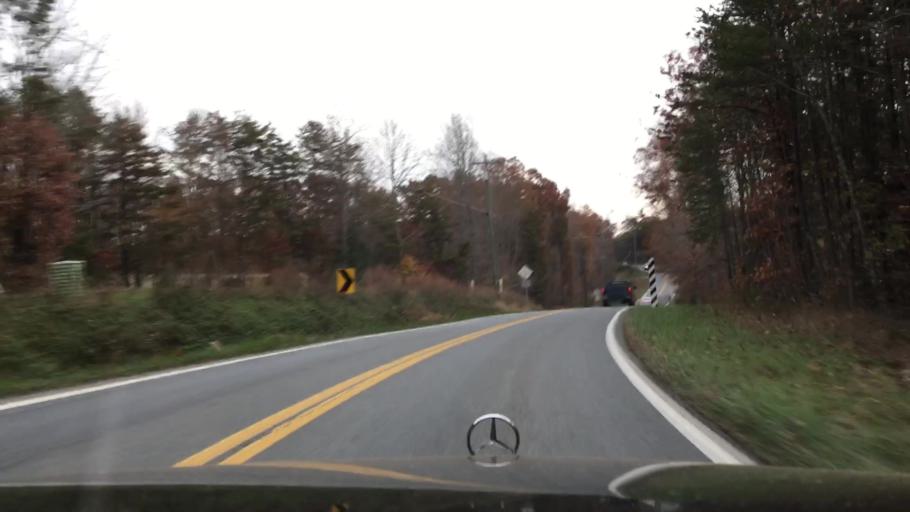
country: US
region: Virginia
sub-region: Campbell County
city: Timberlake
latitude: 37.2560
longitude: -79.2784
